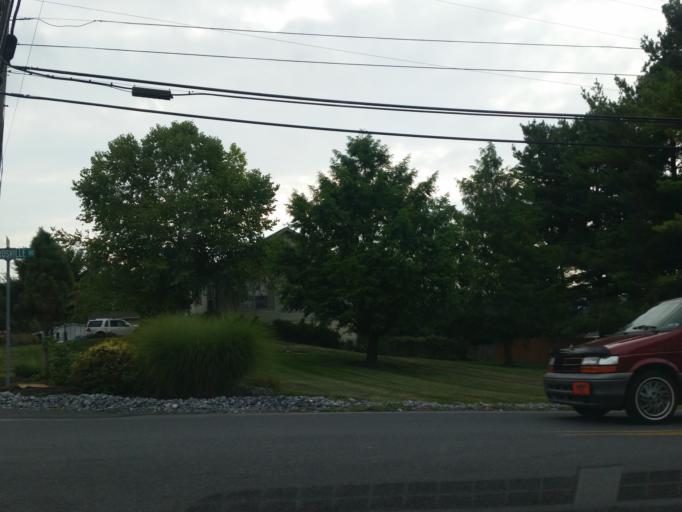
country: US
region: Pennsylvania
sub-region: Lebanon County
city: Richland
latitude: 40.3814
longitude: -76.2693
